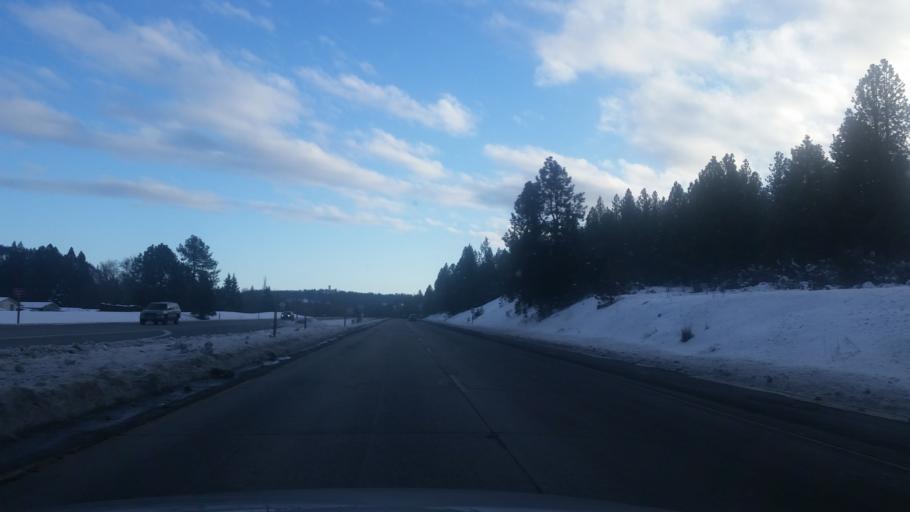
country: US
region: Washington
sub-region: Spokane County
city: Spokane
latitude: 47.6410
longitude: -117.4486
